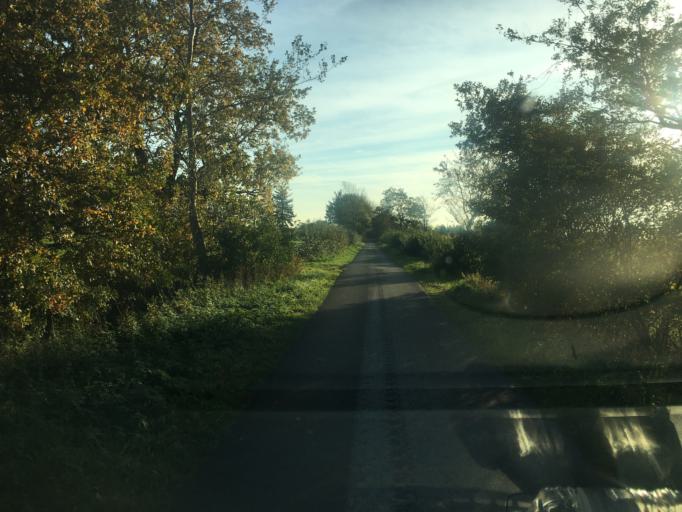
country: DE
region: Schleswig-Holstein
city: Bramstedtlund
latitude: 54.8615
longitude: 9.0787
